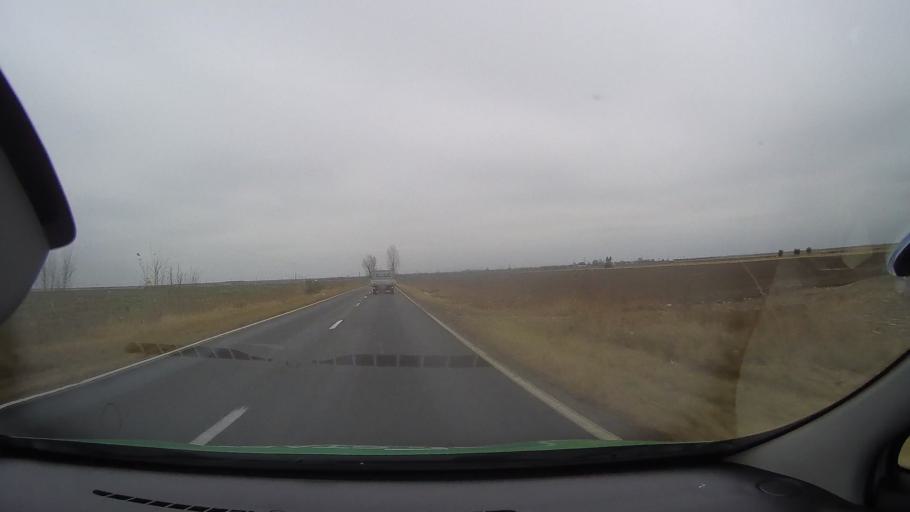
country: RO
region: Ialomita
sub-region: Comuna Scanteia
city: Iazu
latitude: 44.7407
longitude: 27.4391
